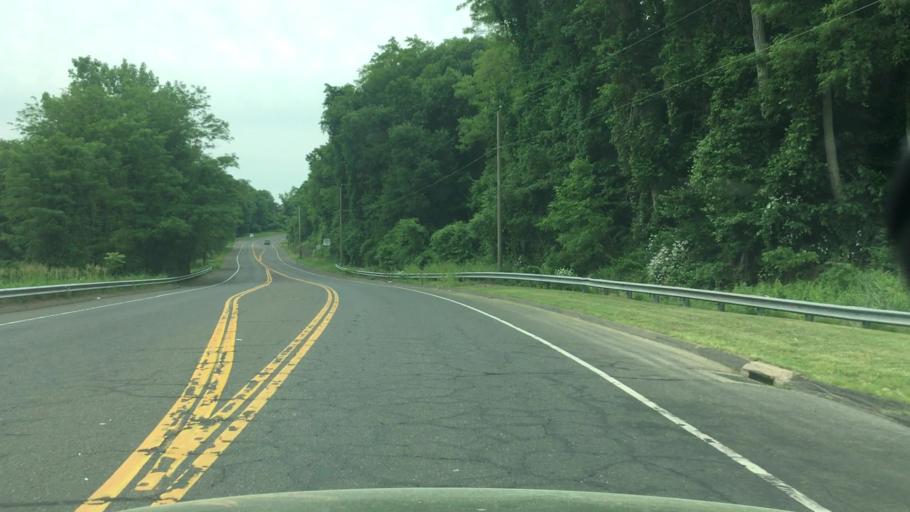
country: US
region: Connecticut
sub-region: Hartford County
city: Windsor Locks
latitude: 41.9026
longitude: -72.6340
